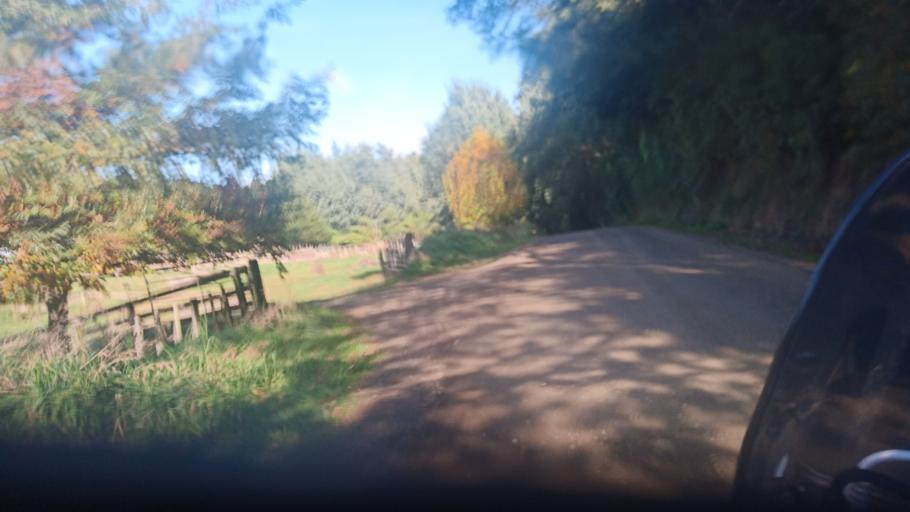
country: NZ
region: Bay of Plenty
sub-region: Opotiki District
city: Opotiki
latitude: -38.4393
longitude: 177.5380
